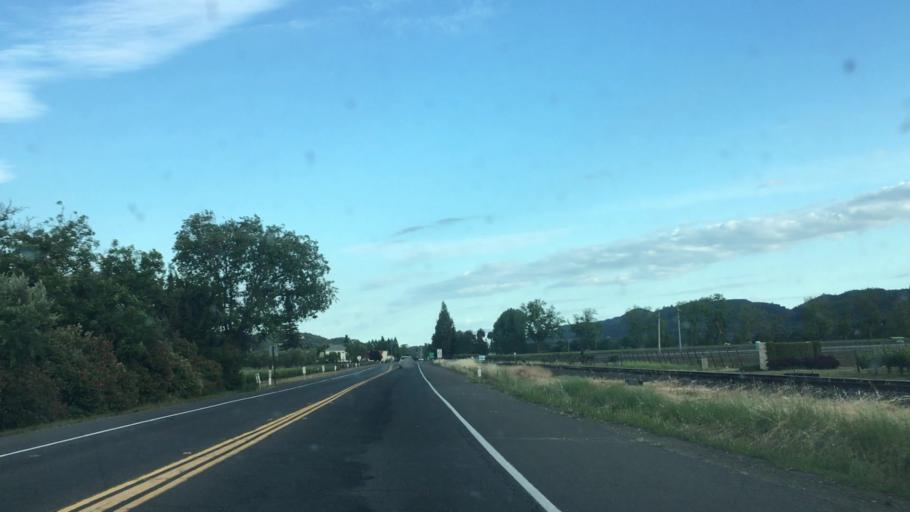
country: US
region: California
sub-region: Napa County
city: Yountville
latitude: 38.4408
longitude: -122.4063
